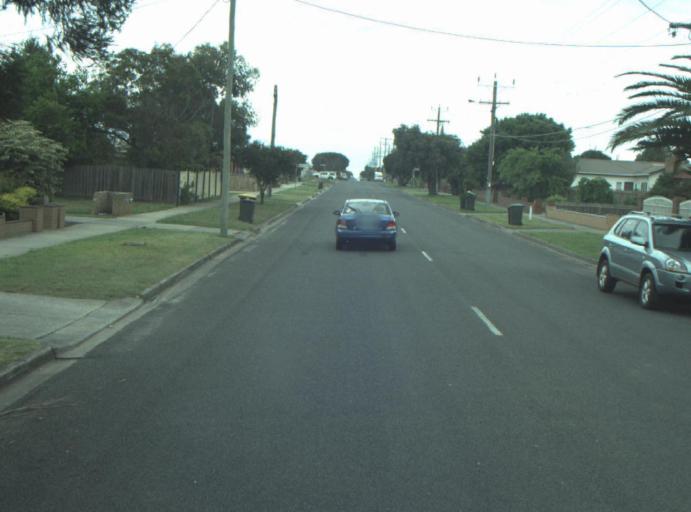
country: AU
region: Victoria
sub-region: Greater Geelong
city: Breakwater
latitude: -38.1816
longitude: 144.3894
